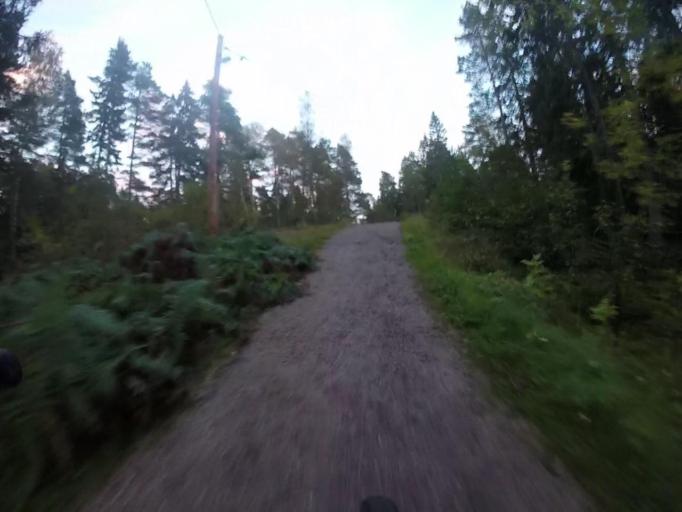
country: SE
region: Vaestra Goetaland
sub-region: Trollhattan
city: Trollhattan
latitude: 58.2950
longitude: 12.2563
